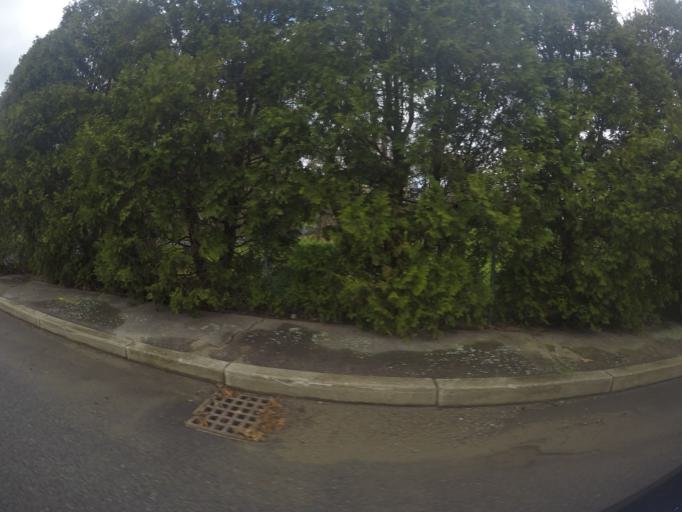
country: US
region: Massachusetts
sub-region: Bristol County
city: Easton
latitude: 42.0318
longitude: -71.1306
